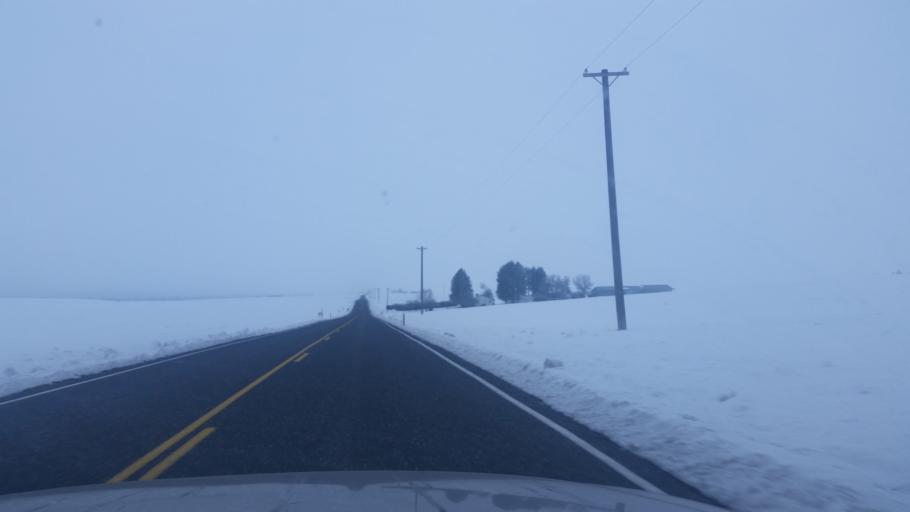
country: US
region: Washington
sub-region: Spokane County
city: Medical Lake
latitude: 47.5925
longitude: -117.8436
